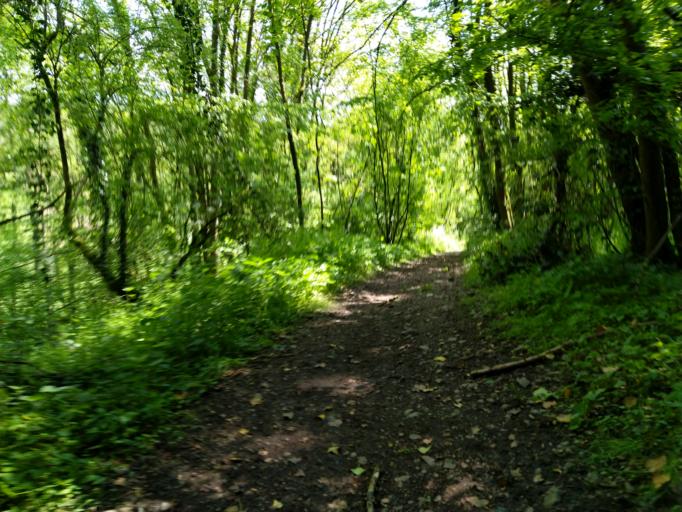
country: BE
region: Wallonia
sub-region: Province du Hainaut
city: Mons
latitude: 50.4950
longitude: 4.0180
